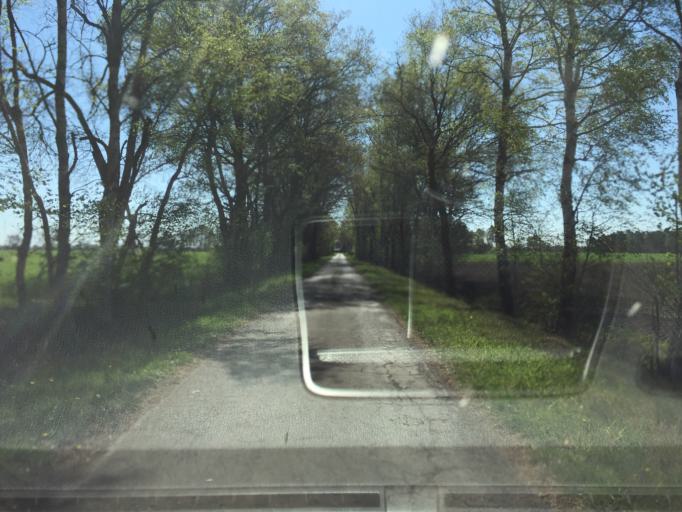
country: DE
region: Lower Saxony
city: Wehrbleck
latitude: 52.5709
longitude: 8.6846
